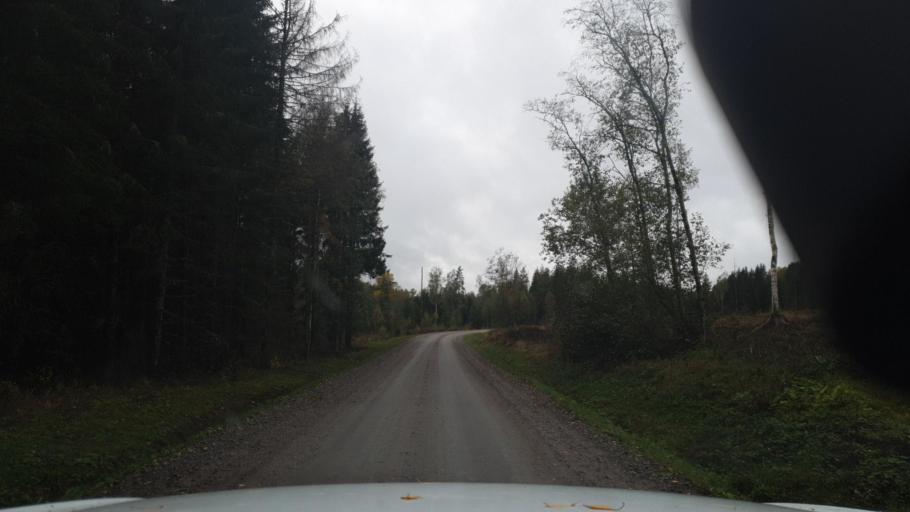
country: SE
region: Vaermland
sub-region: Karlstads Kommun
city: Edsvalla
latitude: 59.5450
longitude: 13.0064
